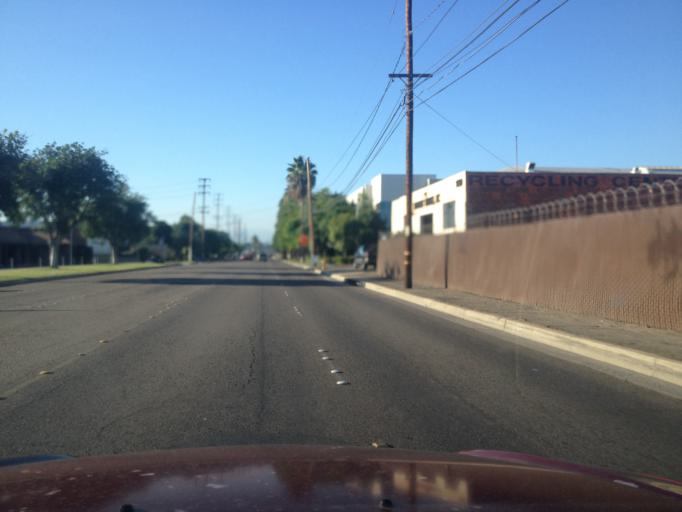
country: US
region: California
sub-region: Orange County
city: Anaheim
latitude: 33.8494
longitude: -117.9198
